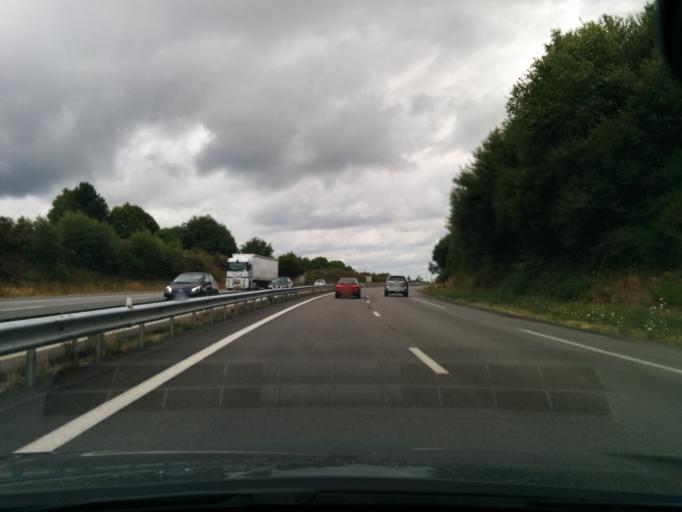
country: FR
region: Limousin
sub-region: Departement de la Haute-Vienne
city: Bessines-sur-Gartempe
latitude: 46.0817
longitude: 1.3565
